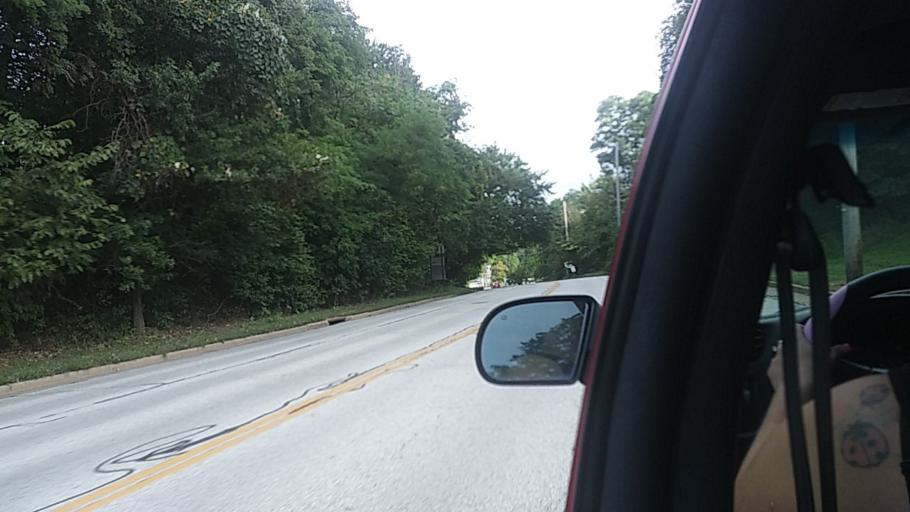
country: US
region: Ohio
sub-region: Summit County
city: Cuyahoga Falls
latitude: 41.1159
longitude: -81.4658
